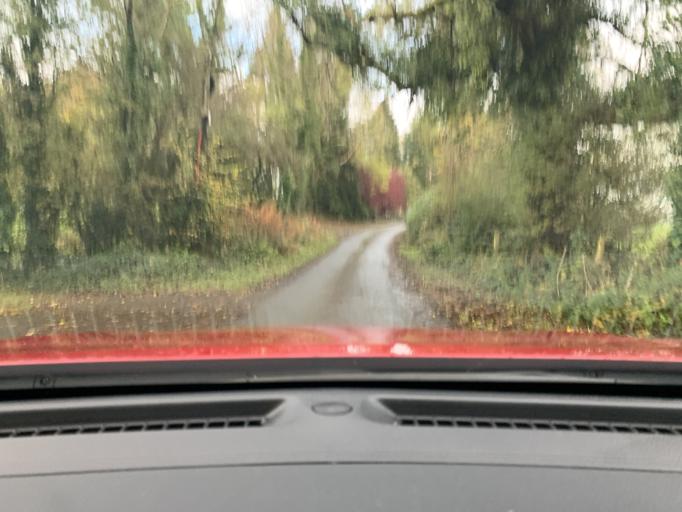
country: IE
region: Connaught
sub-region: Sligo
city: Collooney
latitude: 54.1672
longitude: -8.5188
